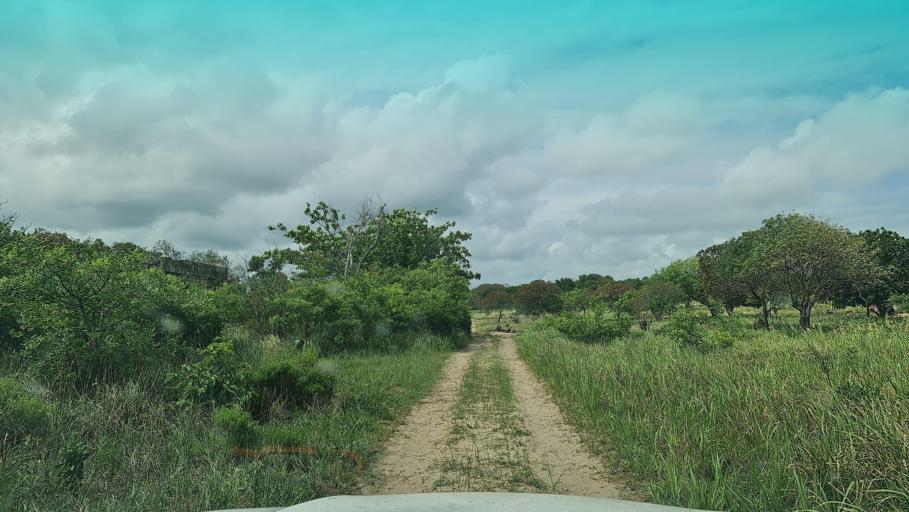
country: MZ
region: Maputo
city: Manhica
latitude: -25.3963
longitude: 33.0283
